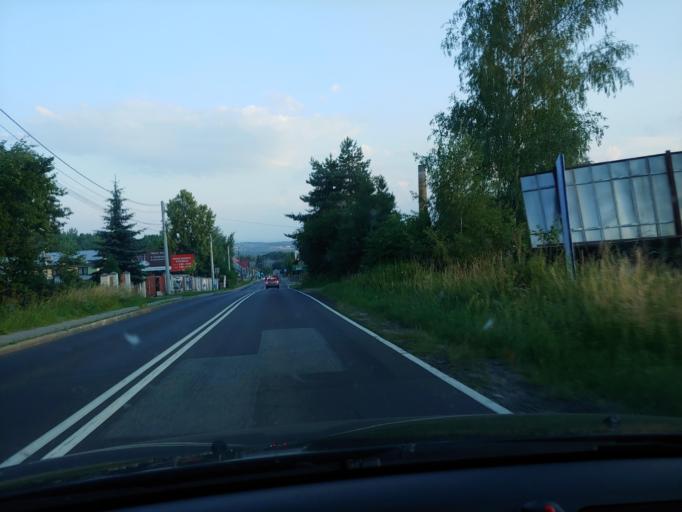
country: PL
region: Lesser Poland Voivodeship
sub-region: Powiat chrzanowski
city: Myslachowice
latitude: 50.1749
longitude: 19.4735
